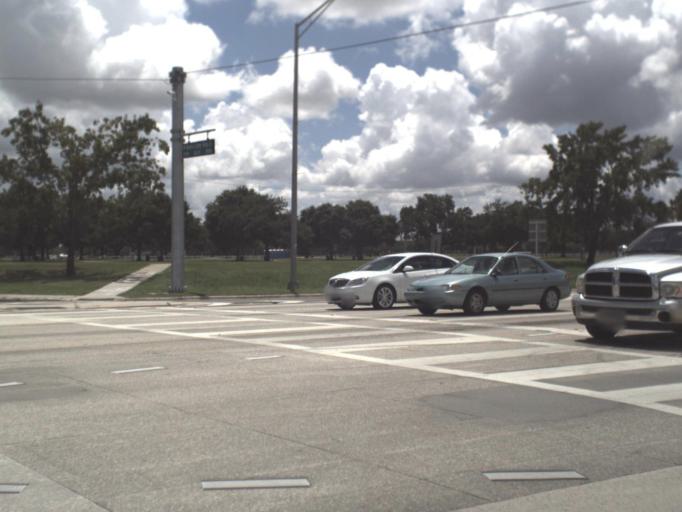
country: US
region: Florida
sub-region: Hillsborough County
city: Egypt Lake-Leto
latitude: 27.9815
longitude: -82.5055
